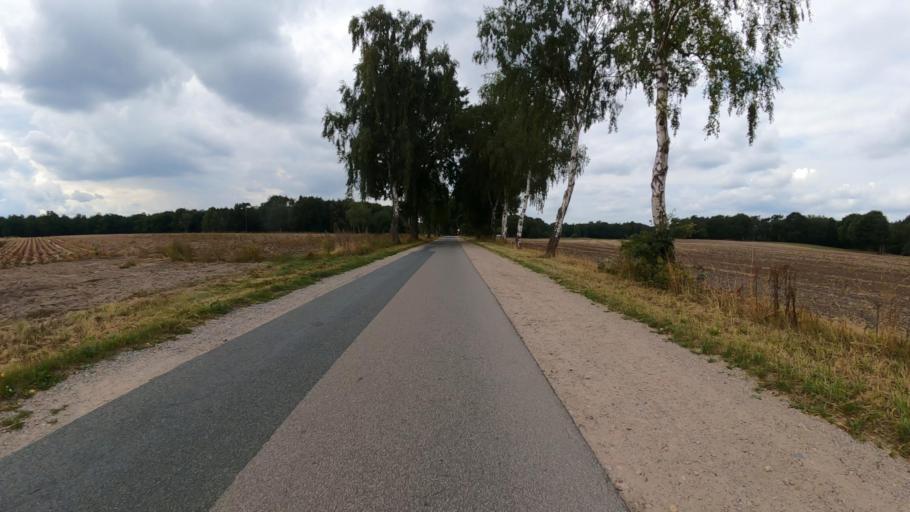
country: DE
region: Lower Saxony
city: Drestedt
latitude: 53.3278
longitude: 9.7545
